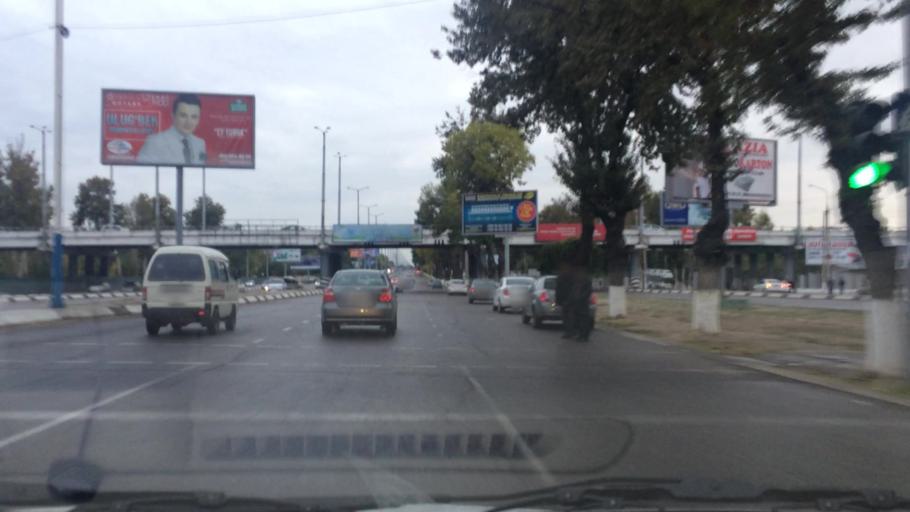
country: UZ
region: Toshkent Shahri
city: Tashkent
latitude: 41.2569
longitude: 69.1937
